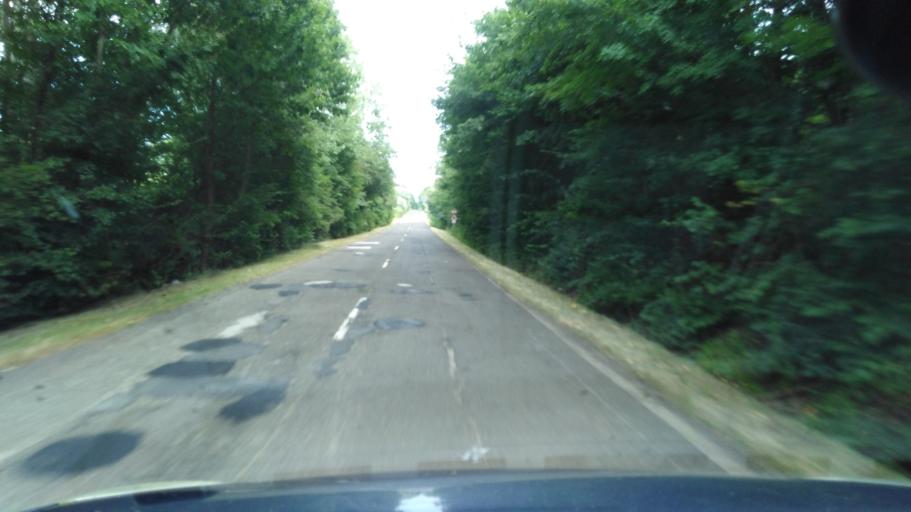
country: HU
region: Nograd
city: Karancskeszi
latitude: 48.2093
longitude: 19.5715
